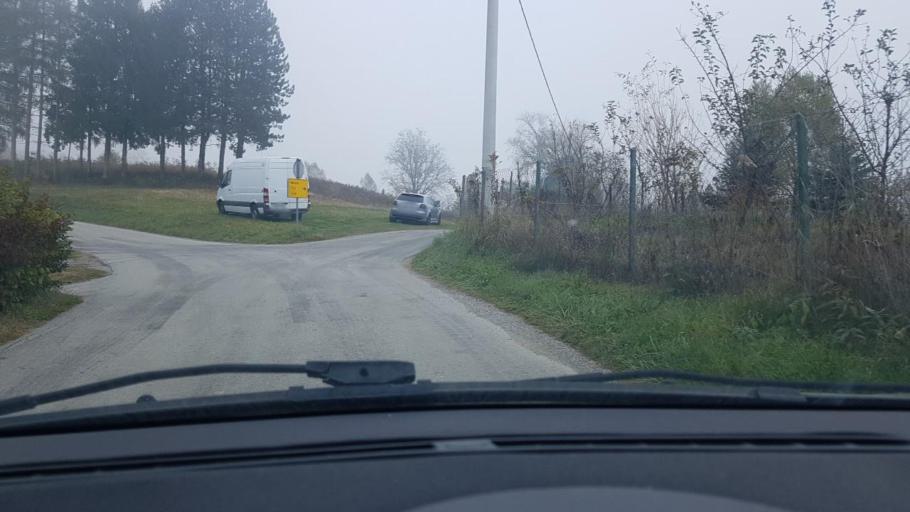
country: HR
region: Krapinsko-Zagorska
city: Mihovljan
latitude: 46.1368
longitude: 15.9770
